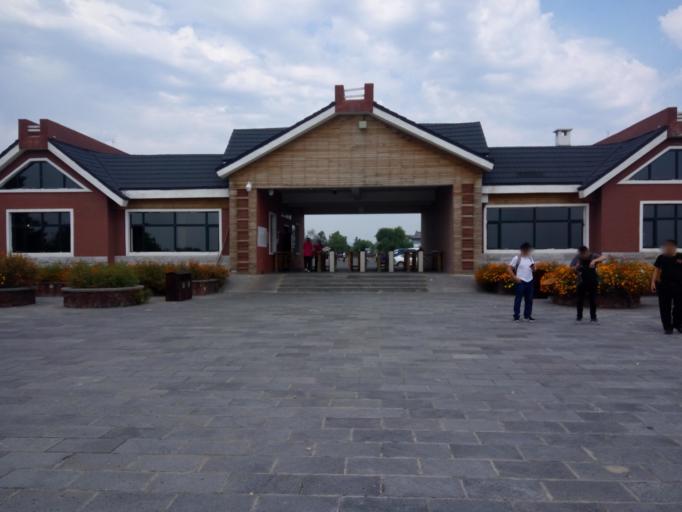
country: CN
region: Heilongjiang Sheng
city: Erjing
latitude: 48.6481
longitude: 126.1490
